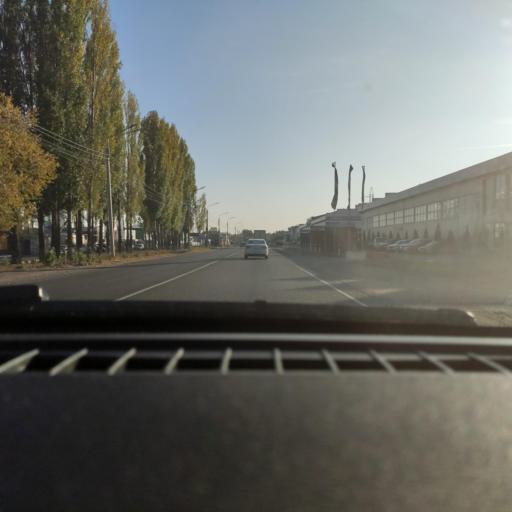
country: RU
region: Voronezj
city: Maslovka
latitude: 51.6404
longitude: 39.2937
